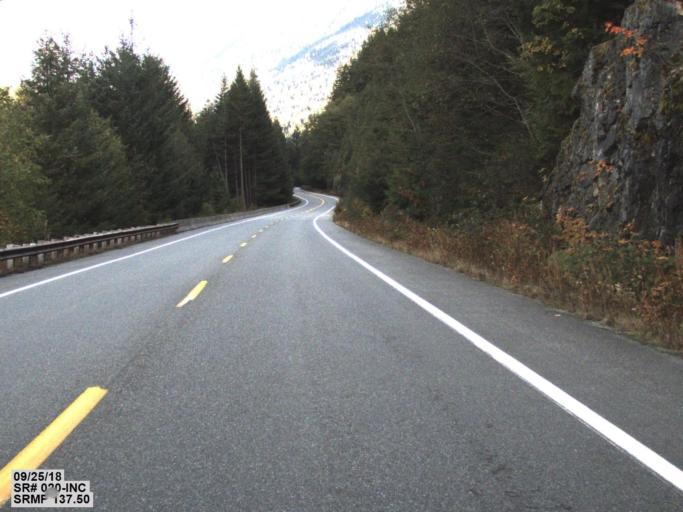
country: US
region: Washington
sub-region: Snohomish County
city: Darrington
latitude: 48.7132
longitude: -120.9950
